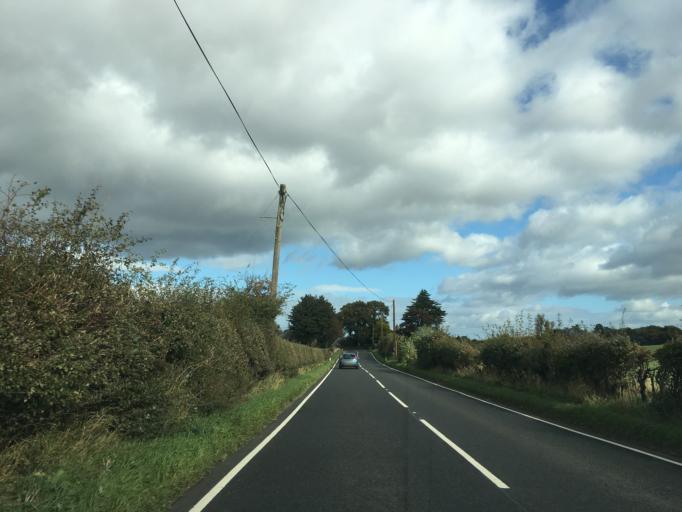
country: GB
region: Scotland
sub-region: Fife
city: Pathhead
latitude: 55.8916
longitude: -2.9716
